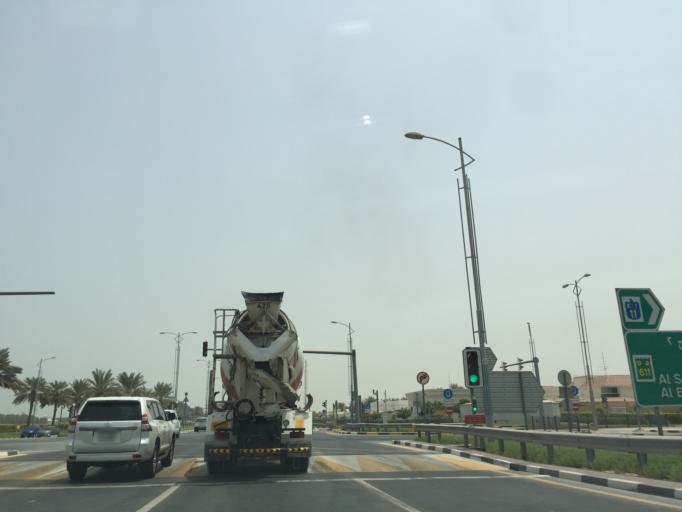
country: AE
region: Dubai
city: Dubai
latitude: 25.1116
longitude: 55.1684
